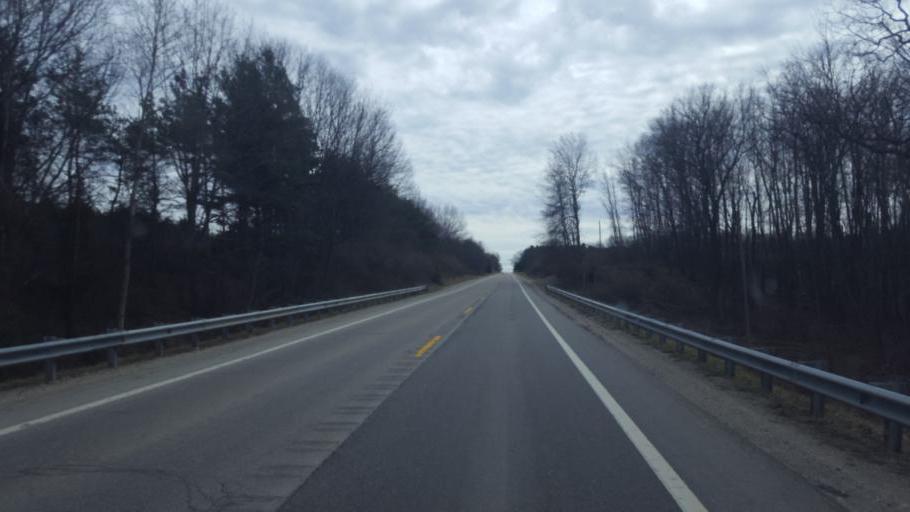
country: US
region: Michigan
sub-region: Isabella County
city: Lake Isabella
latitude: 43.6874
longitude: -85.1466
